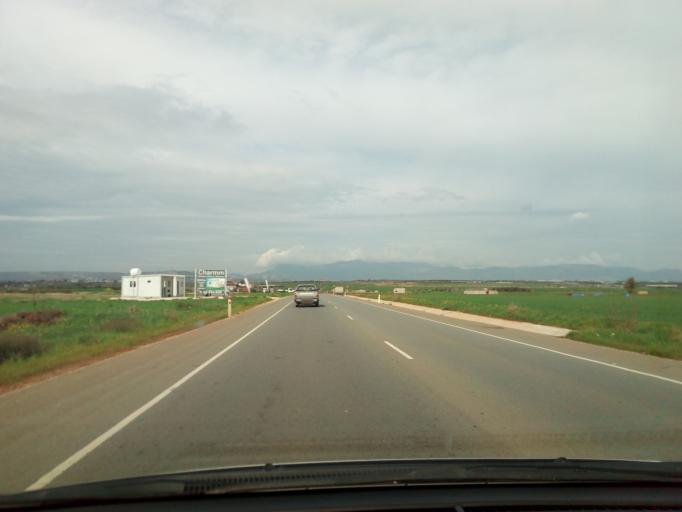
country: CY
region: Lefkosia
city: Akaki
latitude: 35.1473
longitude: 33.1557
